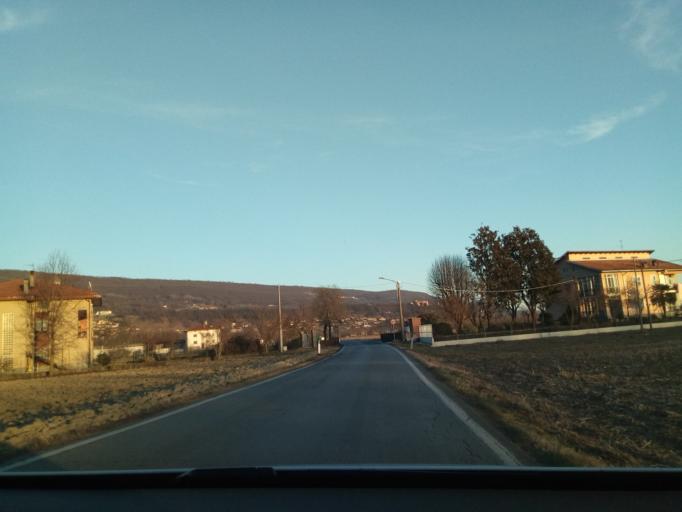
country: IT
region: Piedmont
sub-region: Provincia di Torino
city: Cascinette d'Ivrea
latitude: 45.4790
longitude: 7.9132
